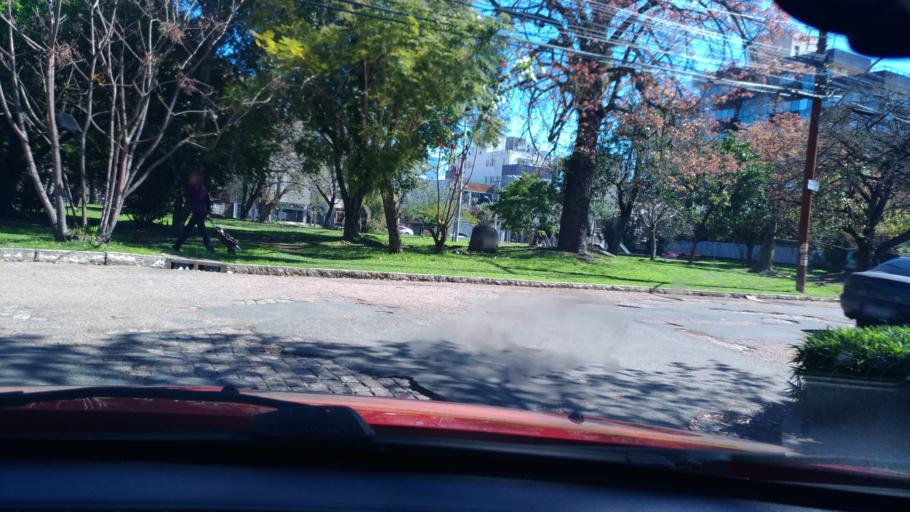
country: BR
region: Rio Grande do Sul
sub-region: Porto Alegre
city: Porto Alegre
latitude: -30.0456
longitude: -51.2037
